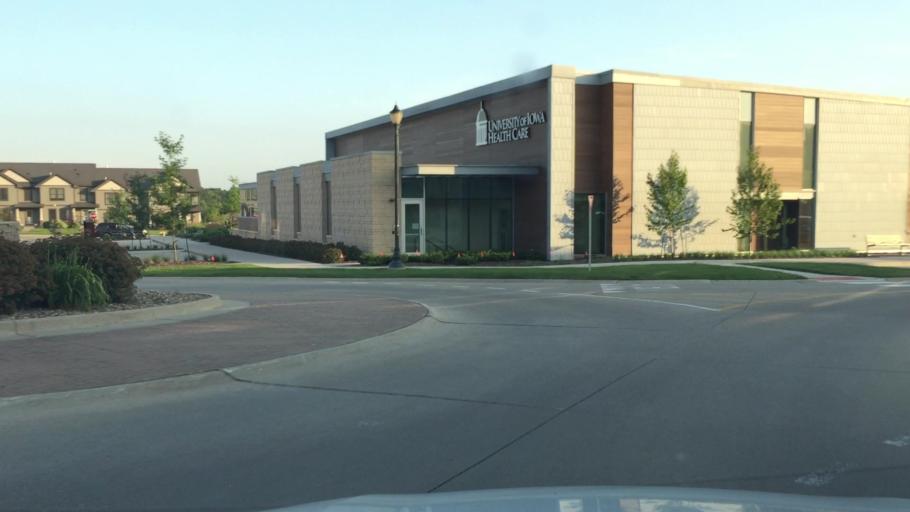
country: US
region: Iowa
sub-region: Johnson County
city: Iowa City
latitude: 41.6685
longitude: -91.4811
